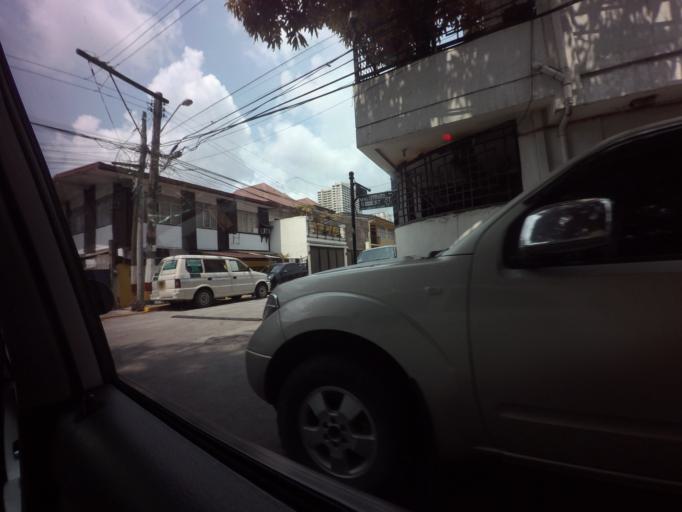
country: PH
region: Metro Manila
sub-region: San Juan
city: San Juan
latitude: 14.5954
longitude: 121.0175
